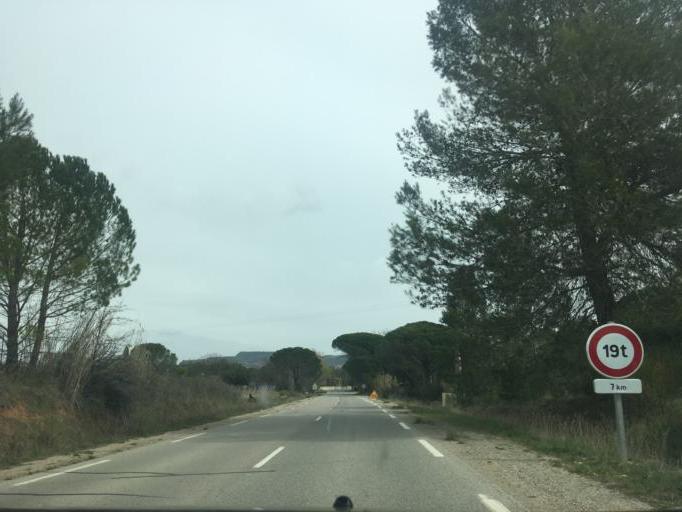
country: FR
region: Provence-Alpes-Cote d'Azur
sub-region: Departement du Var
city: Le Muy
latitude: 43.4944
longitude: 6.5732
